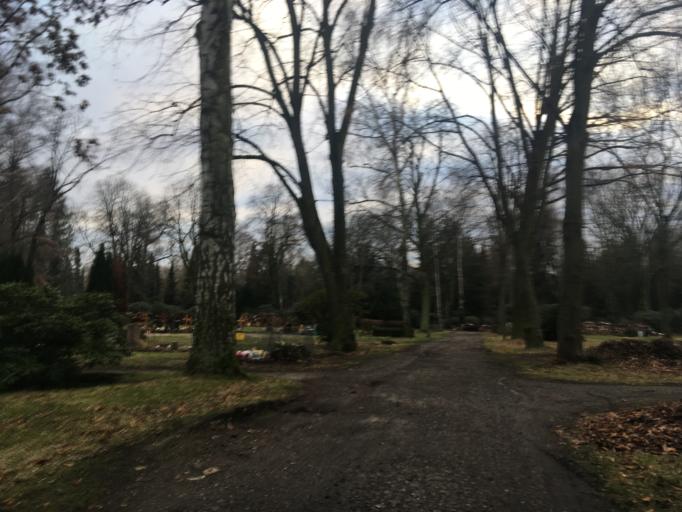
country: DE
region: Berlin
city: Reinickendorf
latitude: 52.5682
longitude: 13.3355
